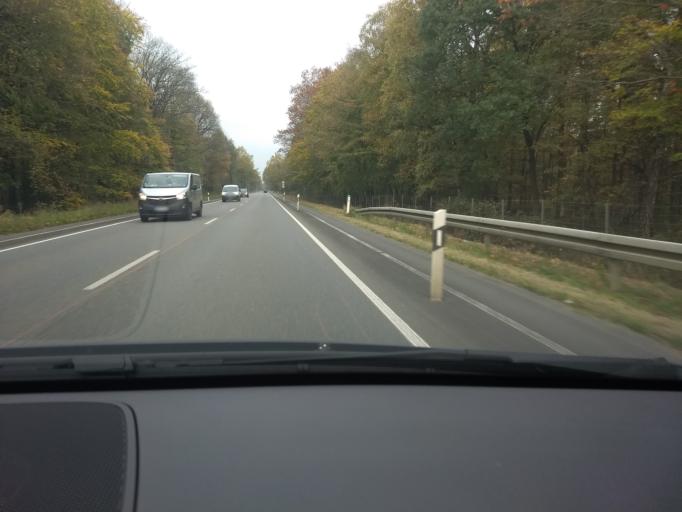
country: DE
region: North Rhine-Westphalia
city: Dorsten
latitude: 51.7103
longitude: 6.9272
